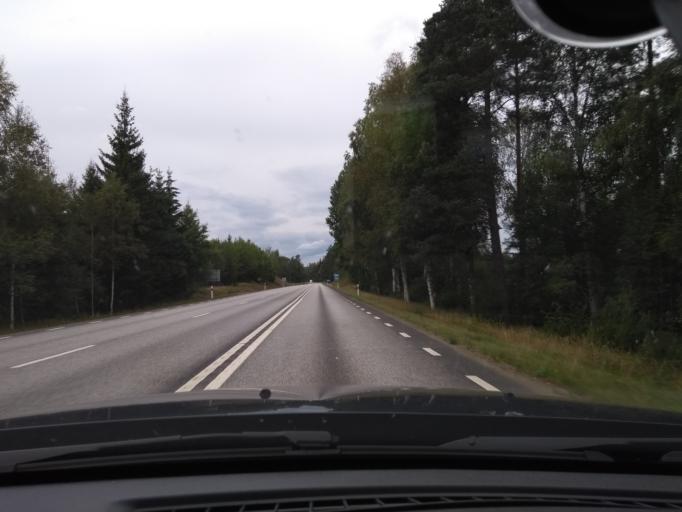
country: SE
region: Joenkoeping
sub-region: Eksjo Kommun
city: Haljarp
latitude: 57.6328
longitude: 15.4259
